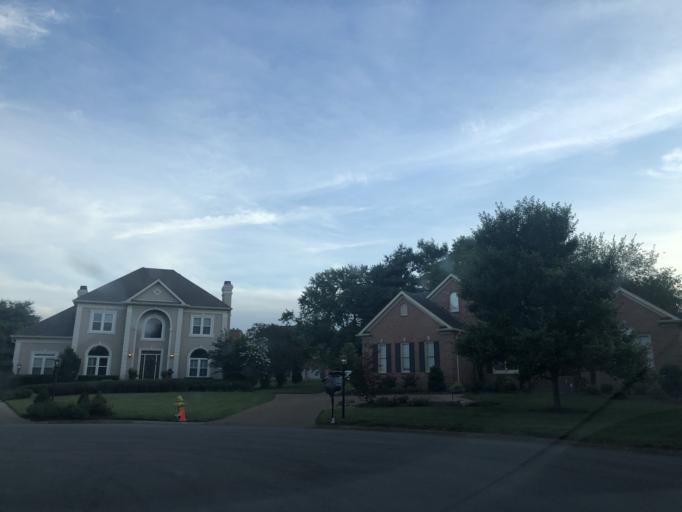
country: US
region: Tennessee
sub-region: Davidson County
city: Belle Meade
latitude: 36.0484
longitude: -86.9250
